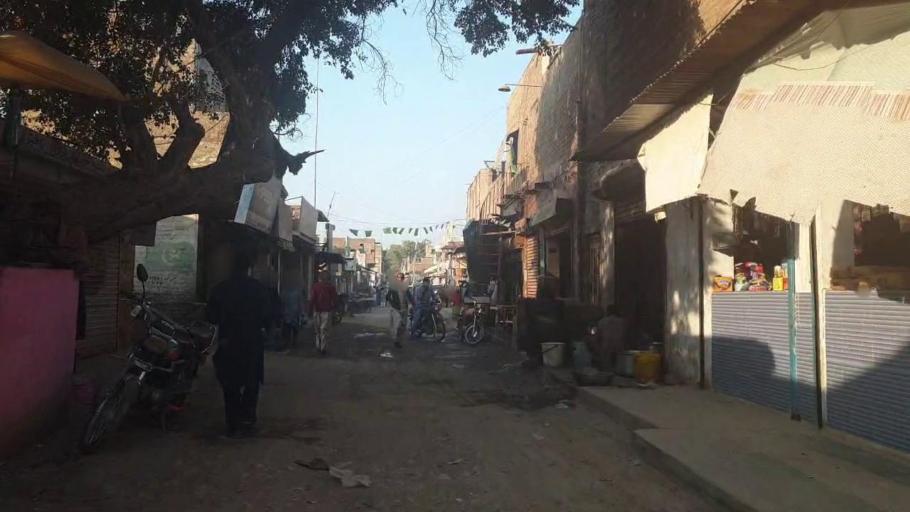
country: PK
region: Sindh
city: Jamshoro
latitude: 25.4440
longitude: 68.2960
